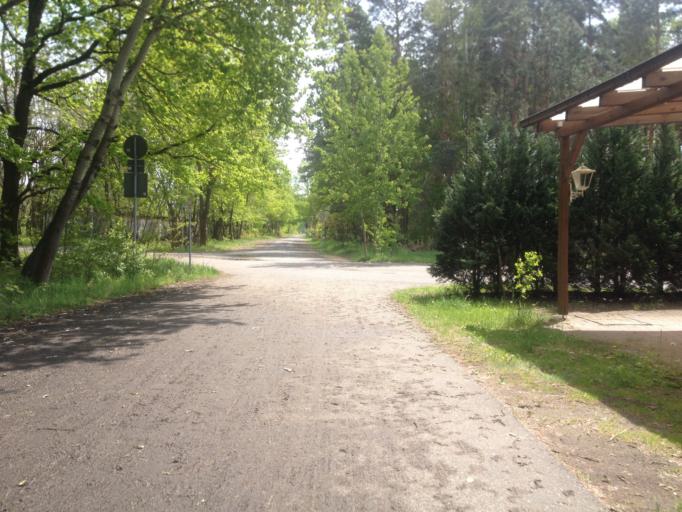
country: DE
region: Brandenburg
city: Cottbus
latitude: 51.7971
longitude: 14.2951
